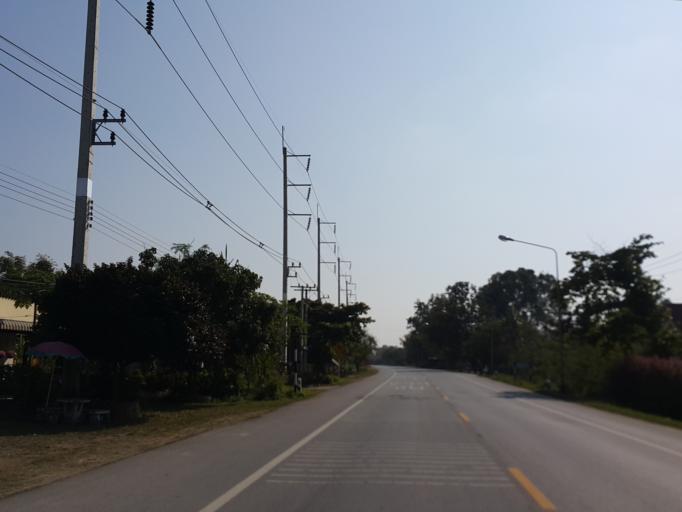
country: TH
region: Lampang
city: Chae Hom
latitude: 18.6761
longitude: 99.5484
